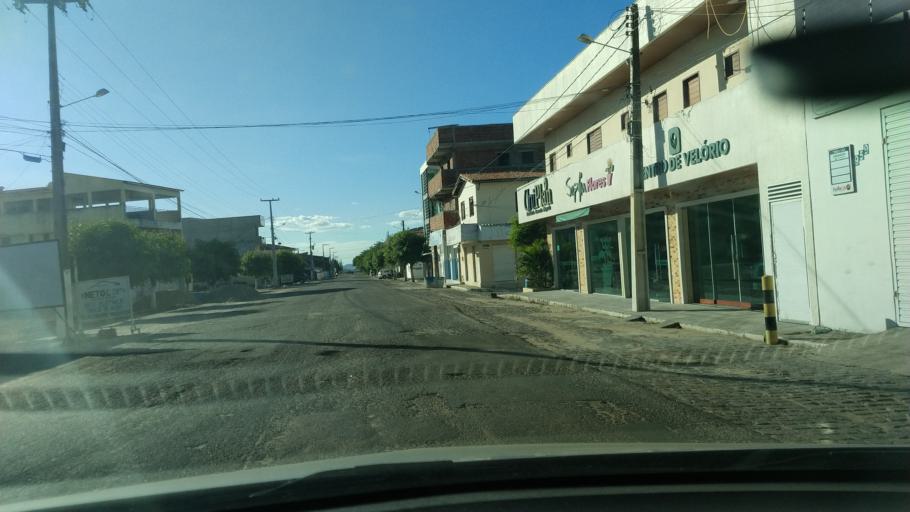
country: BR
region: Rio Grande do Norte
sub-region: Sao Jose Do Campestre
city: Sao Jose do Campestre
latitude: -6.4323
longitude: -35.6447
